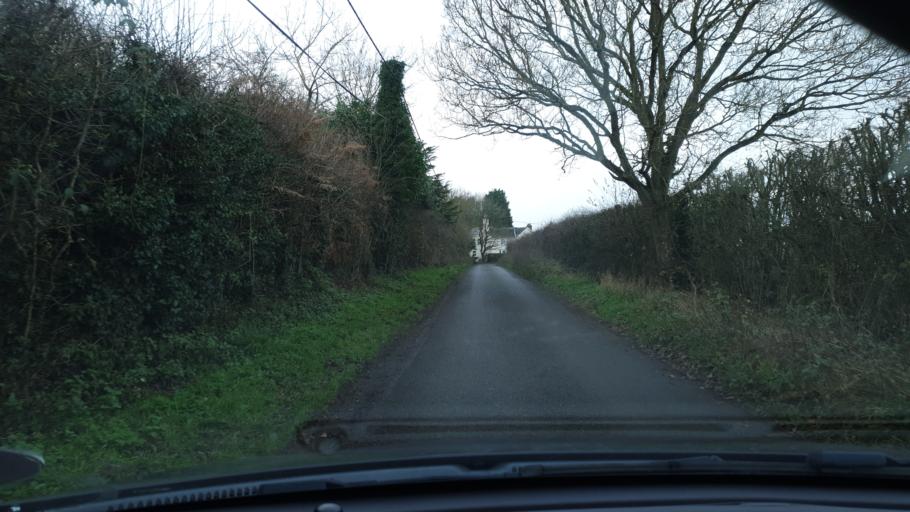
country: GB
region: England
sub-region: Essex
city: Alresford
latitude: 51.8572
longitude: 0.9931
